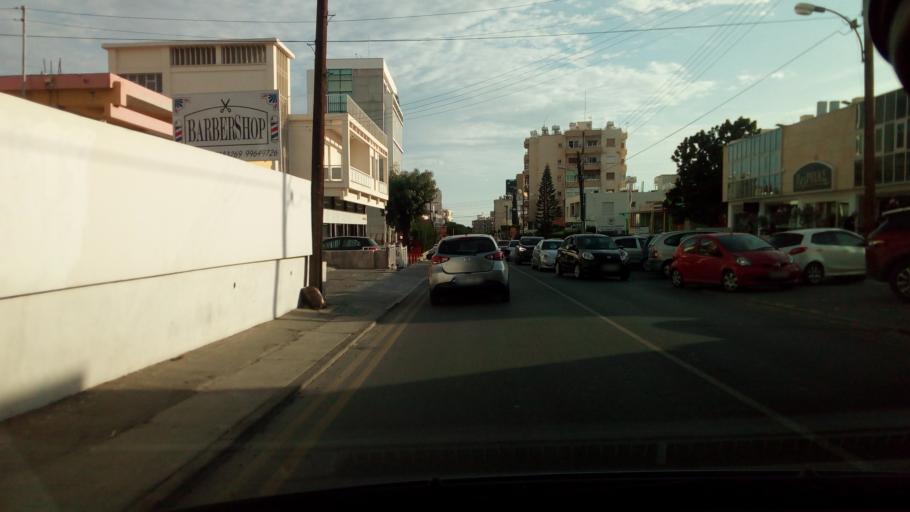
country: CY
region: Limassol
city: Limassol
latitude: 34.6909
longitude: 33.0358
